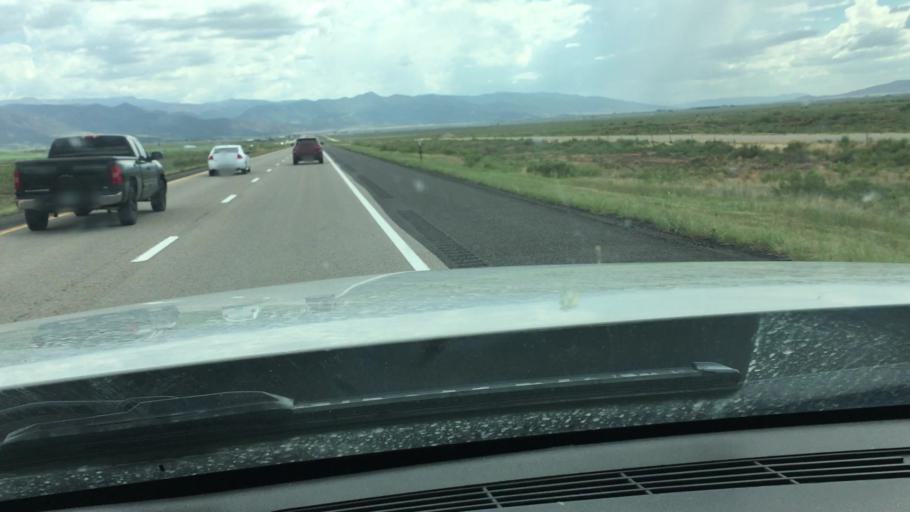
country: US
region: Utah
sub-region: Iron County
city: Parowan
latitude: 37.9564
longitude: -112.7518
